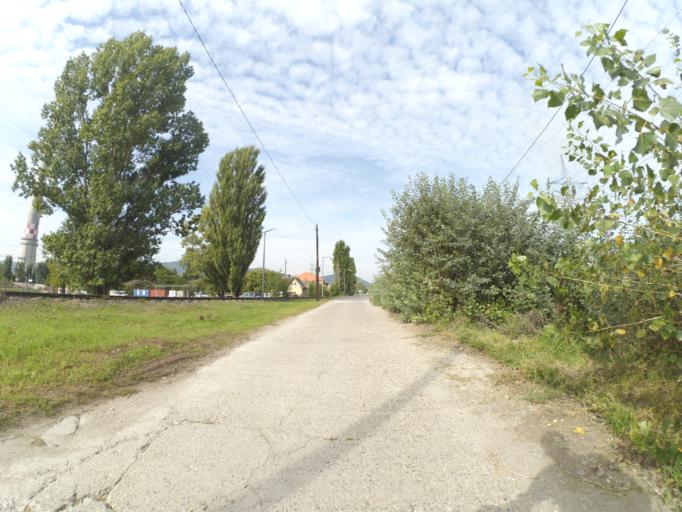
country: HU
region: Budapest
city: Budapest III. keruelet
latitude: 47.5668
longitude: 19.0410
